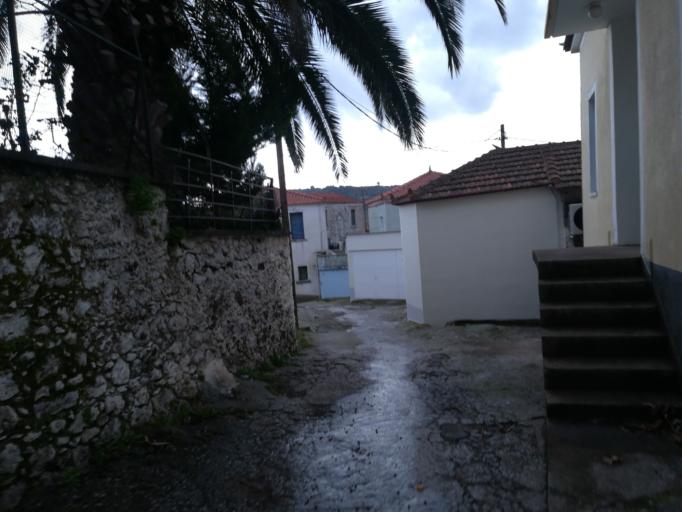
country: GR
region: North Aegean
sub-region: Nomos Lesvou
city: Agia Paraskevi
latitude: 39.2489
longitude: 26.2709
